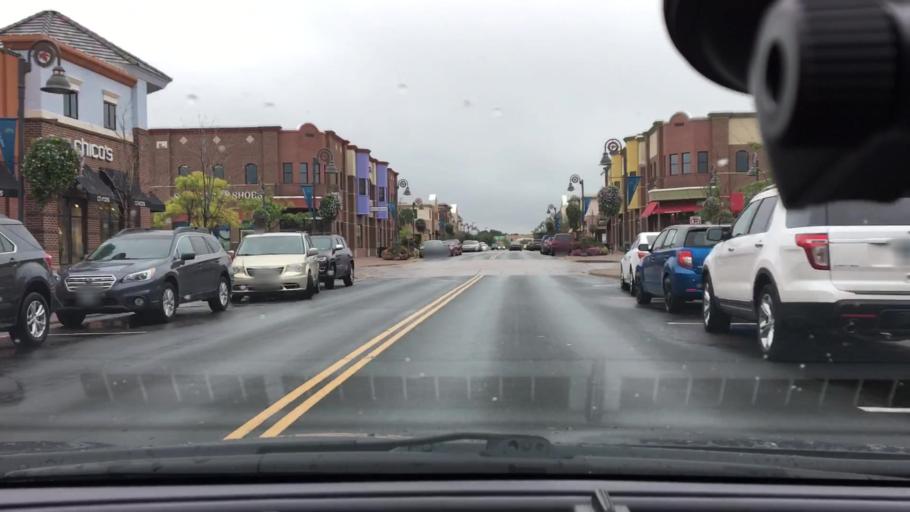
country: US
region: Minnesota
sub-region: Hennepin County
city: Maple Grove
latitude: 45.0962
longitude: -93.4417
